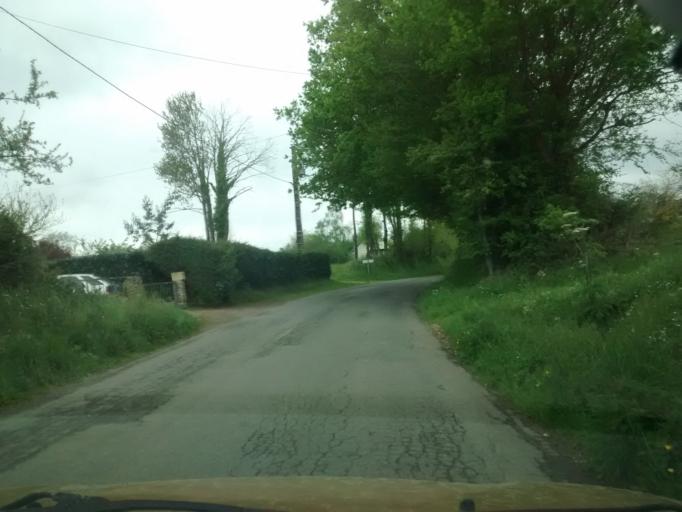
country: FR
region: Brittany
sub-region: Departement du Morbihan
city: Molac
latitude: 47.7207
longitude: -2.4302
